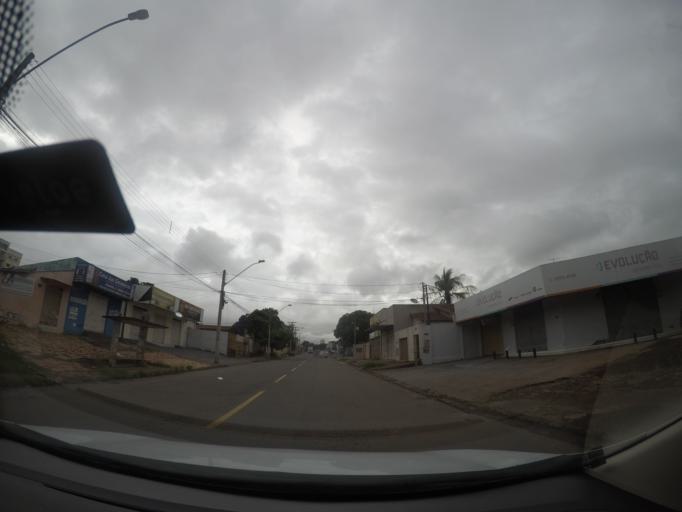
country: BR
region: Goias
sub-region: Goiania
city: Goiania
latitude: -16.7112
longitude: -49.2913
